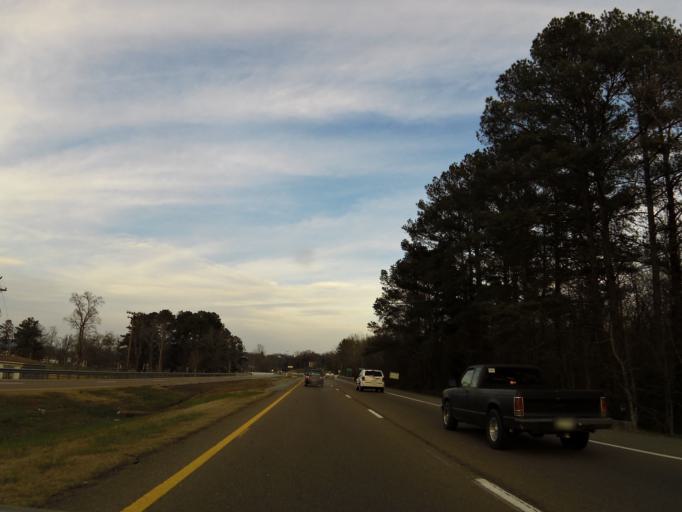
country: US
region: Tennessee
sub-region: Rhea County
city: Dayton
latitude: 35.4868
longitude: -85.0157
